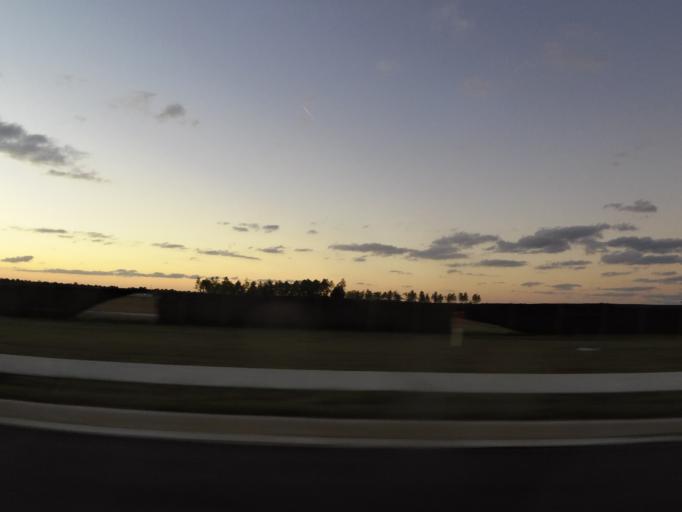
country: US
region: Florida
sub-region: Saint Johns County
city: Palm Valley
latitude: 30.0813
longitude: -81.4771
